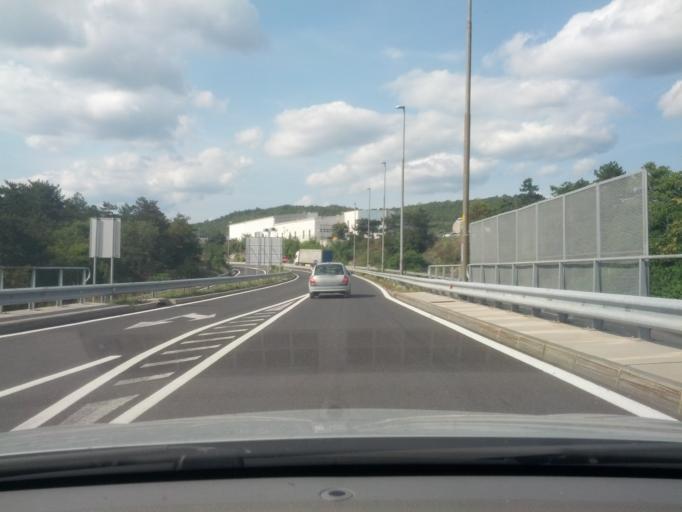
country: SI
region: Sezana
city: Sezana
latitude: 45.7050
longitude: 13.8559
